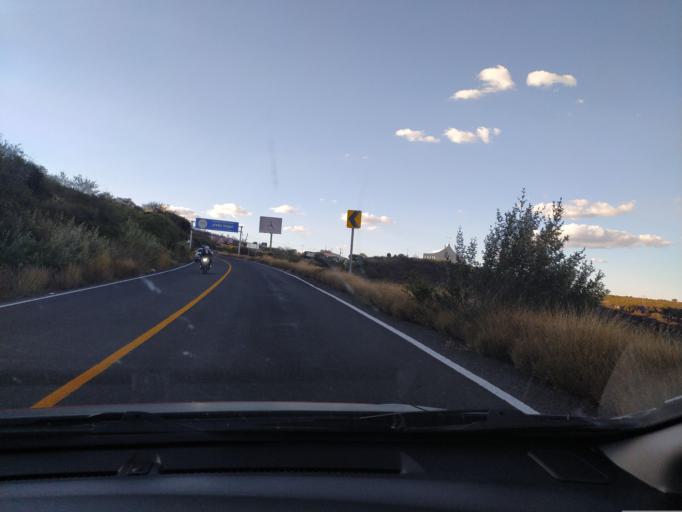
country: MX
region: Guanajuato
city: San Francisco del Rincon
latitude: 21.0304
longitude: -101.9007
